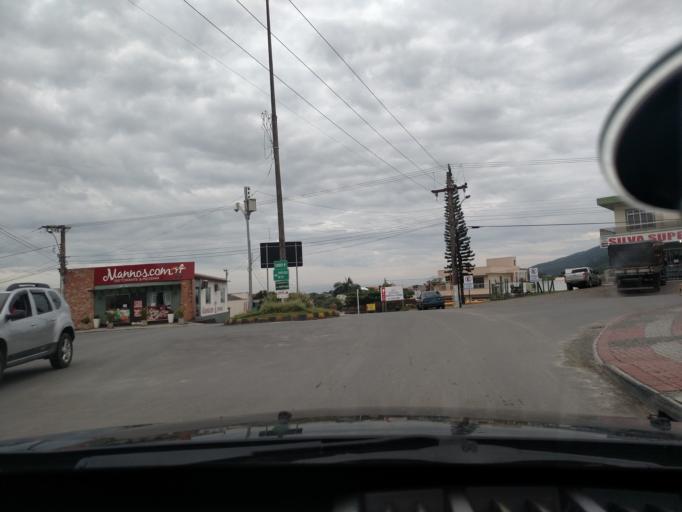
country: BR
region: Santa Catarina
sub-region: Porto Belo
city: Porto Belo
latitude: -27.1725
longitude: -48.5220
